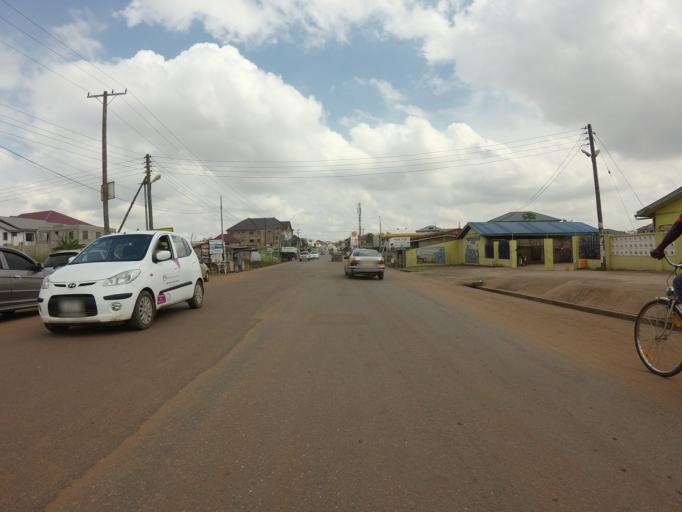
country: GH
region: Greater Accra
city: Nungua
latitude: 5.6207
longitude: -0.0913
